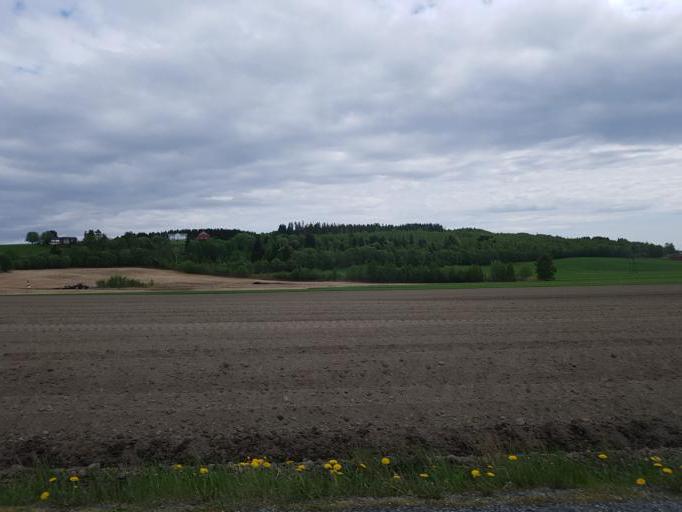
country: NO
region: Nord-Trondelag
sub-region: Levanger
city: Skogn
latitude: 63.6964
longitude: 11.2248
